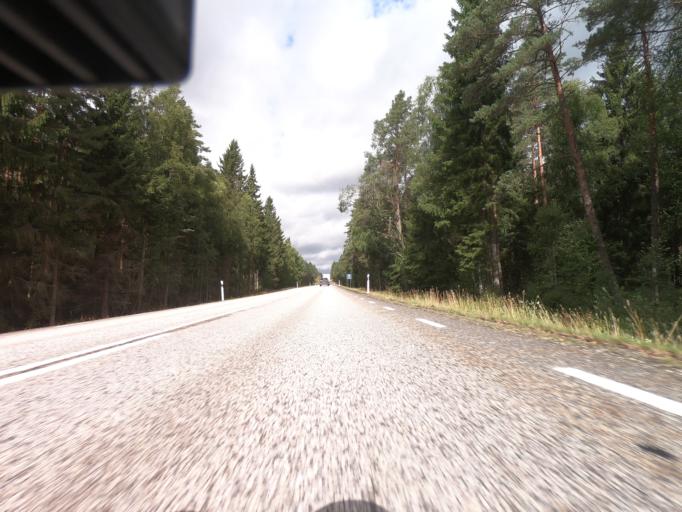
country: SE
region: Joenkoeping
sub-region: Vaggeryds Kommun
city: Vaggeryd
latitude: 57.5602
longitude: 14.2551
